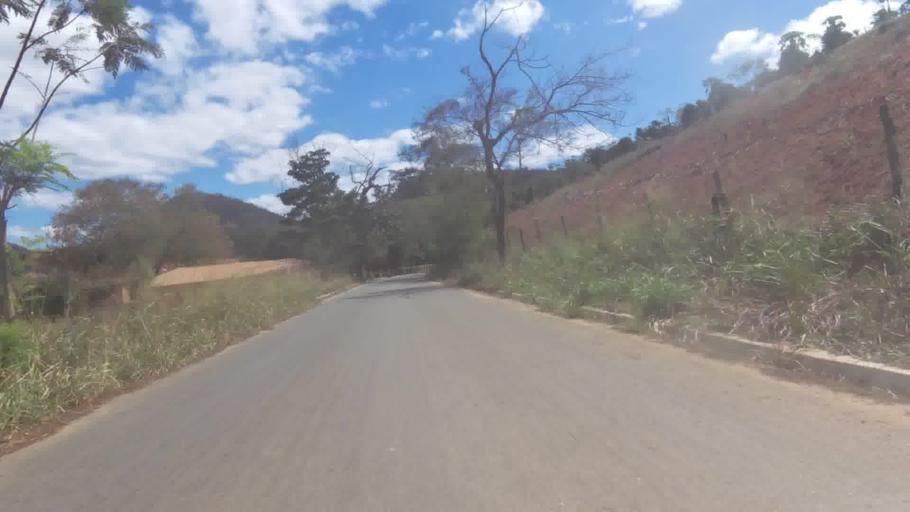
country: BR
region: Espirito Santo
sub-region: Cachoeiro De Itapemirim
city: Cachoeiro de Itapemirim
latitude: -20.9388
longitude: -41.2213
